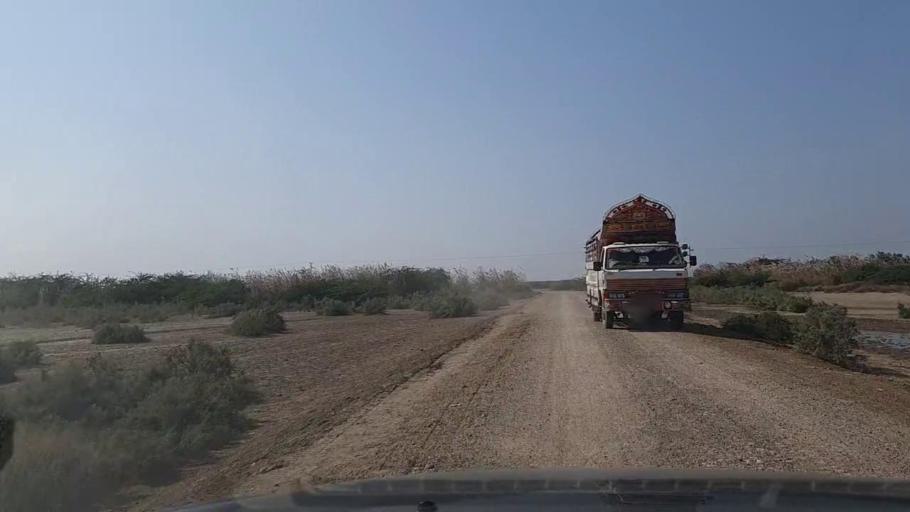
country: PK
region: Sindh
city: Mirpur Sakro
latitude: 24.4260
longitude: 67.7105
